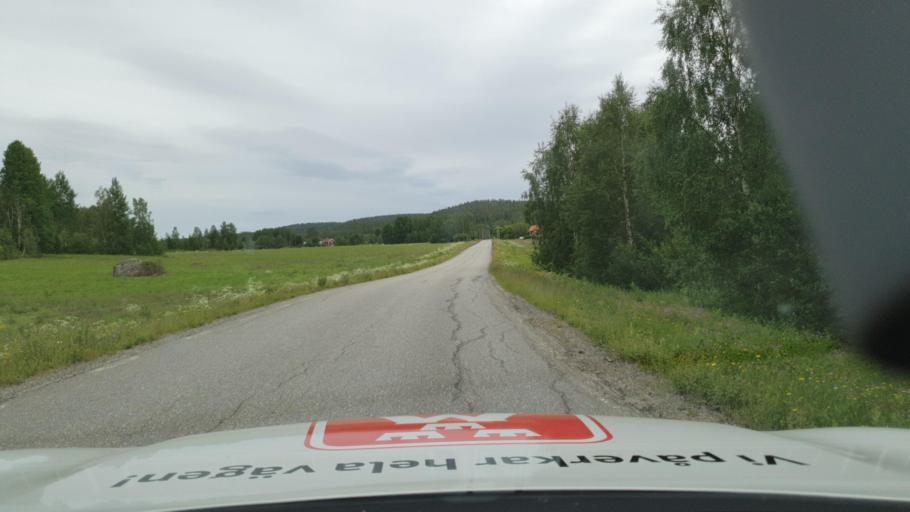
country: SE
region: Vaesterbotten
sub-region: Skelleftea Kommun
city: Burtraesk
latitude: 64.3035
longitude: 20.6496
